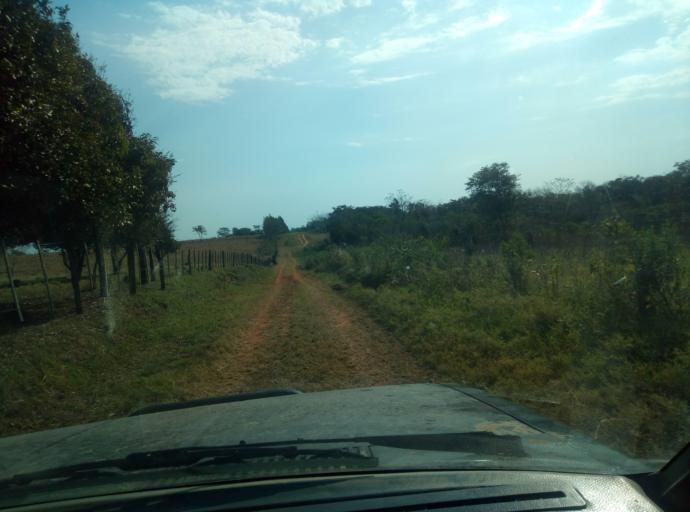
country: PY
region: Caaguazu
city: Doctor Cecilio Baez
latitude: -25.1417
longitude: -56.2576
